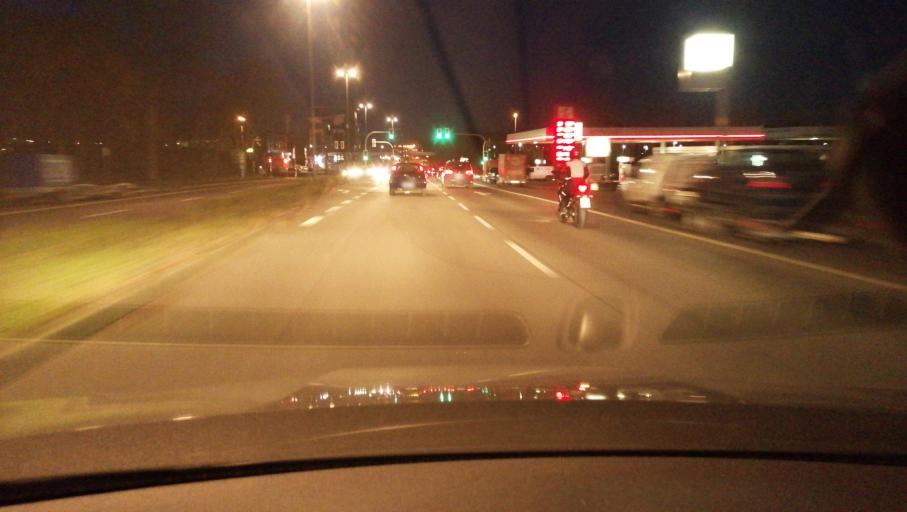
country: DE
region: North Rhine-Westphalia
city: Bochum-Hordel
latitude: 51.5106
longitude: 7.1901
